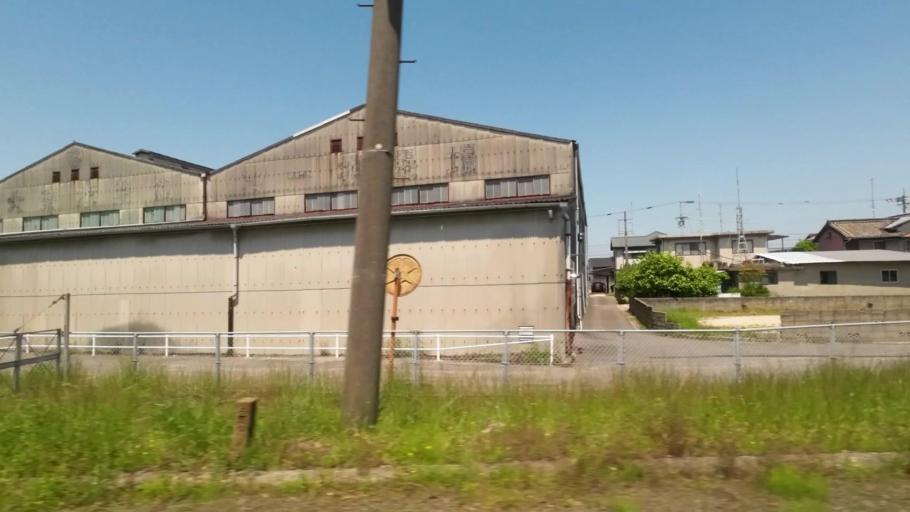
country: JP
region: Ehime
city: Hojo
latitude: 34.0103
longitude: 132.8031
